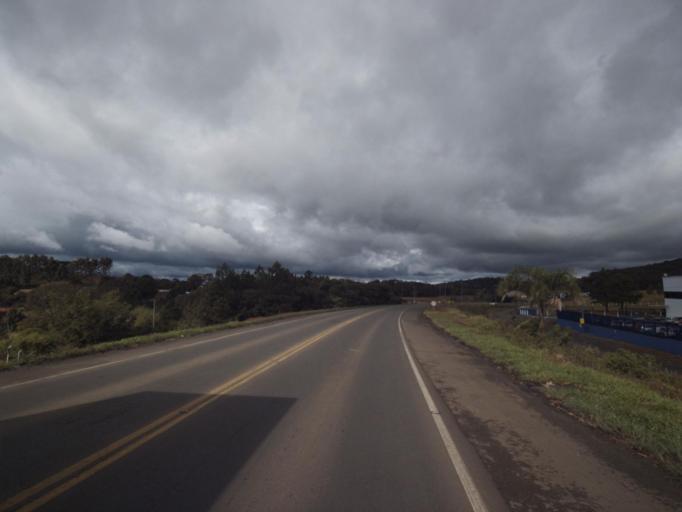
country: BR
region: Santa Catarina
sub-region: Concordia
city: Concordia
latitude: -27.2219
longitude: -51.9488
